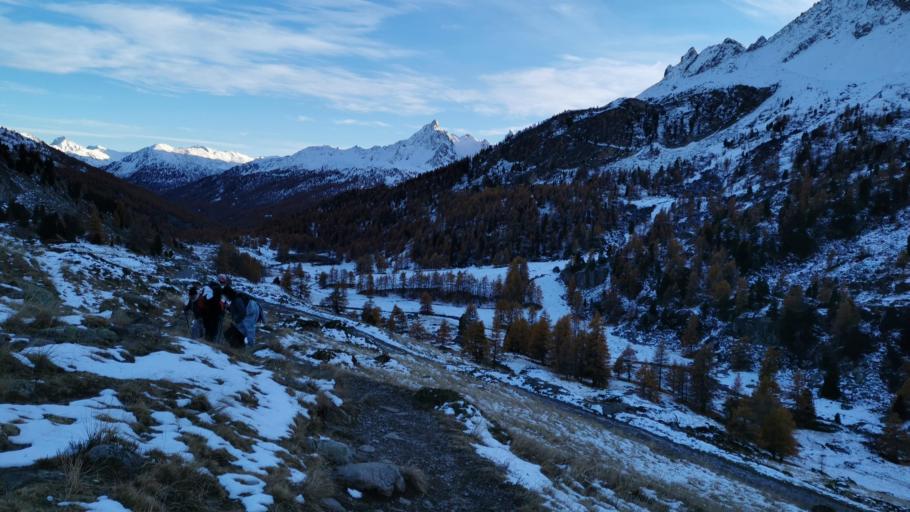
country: FR
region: Provence-Alpes-Cote d'Azur
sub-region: Departement des Hautes-Alpes
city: Le Monetier-les-Bains
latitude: 45.0674
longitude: 6.5186
